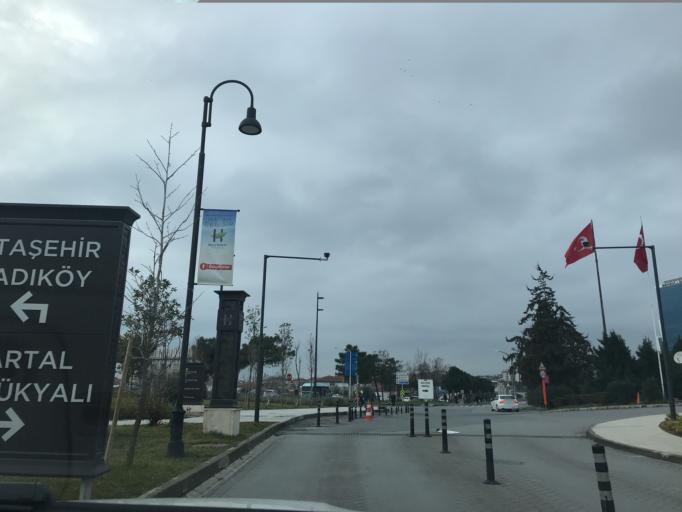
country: TR
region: Istanbul
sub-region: Atasehir
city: Atasehir
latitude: 40.9519
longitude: 29.1202
